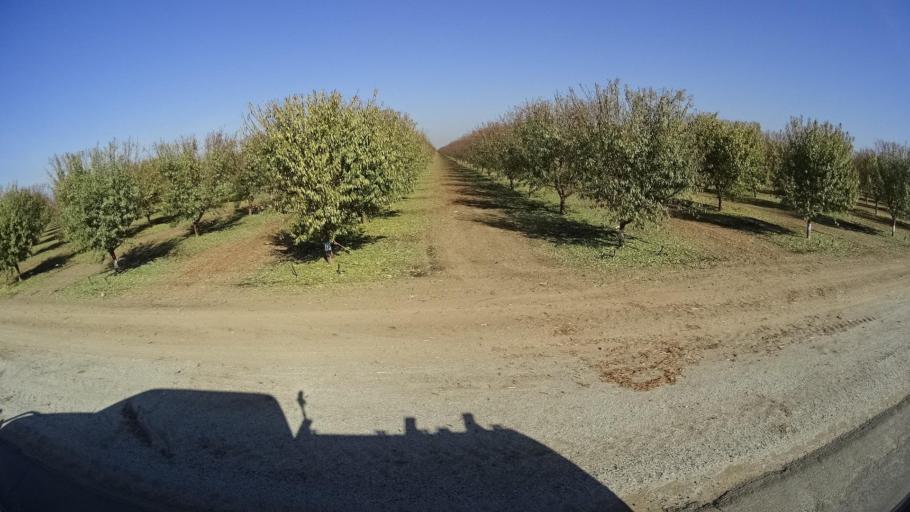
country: US
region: California
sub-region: Kern County
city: McFarland
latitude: 35.7180
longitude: -119.2148
